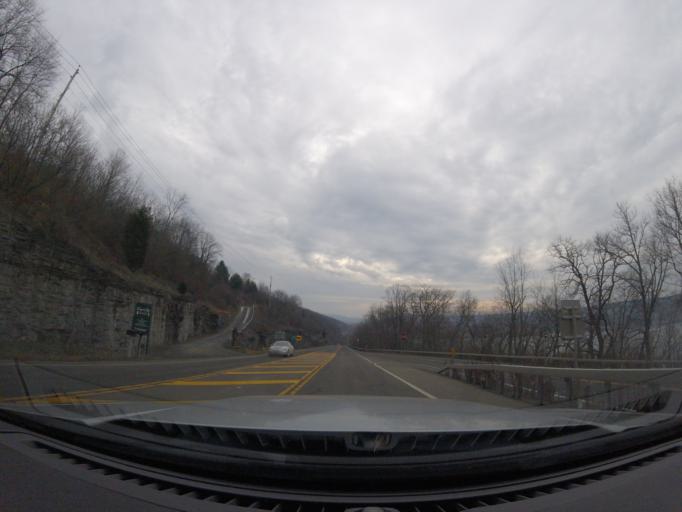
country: US
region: New York
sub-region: Schuyler County
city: Watkins Glen
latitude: 42.3955
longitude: -76.8572
